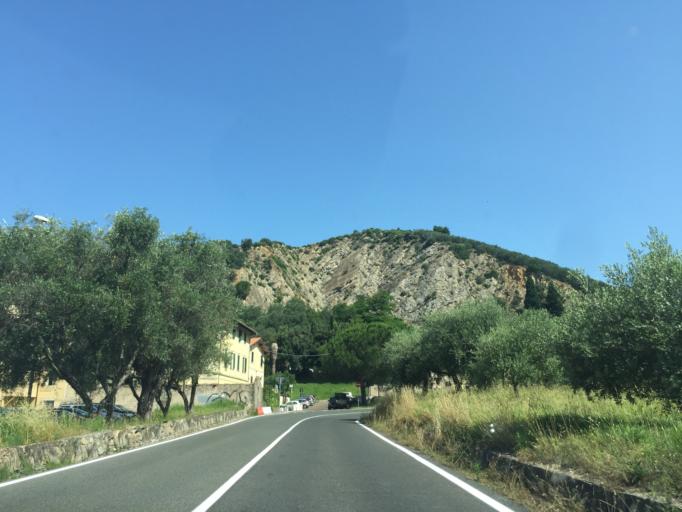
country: IT
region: Tuscany
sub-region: Province of Pisa
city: San Giuliano Terme
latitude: 43.7630
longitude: 10.4446
